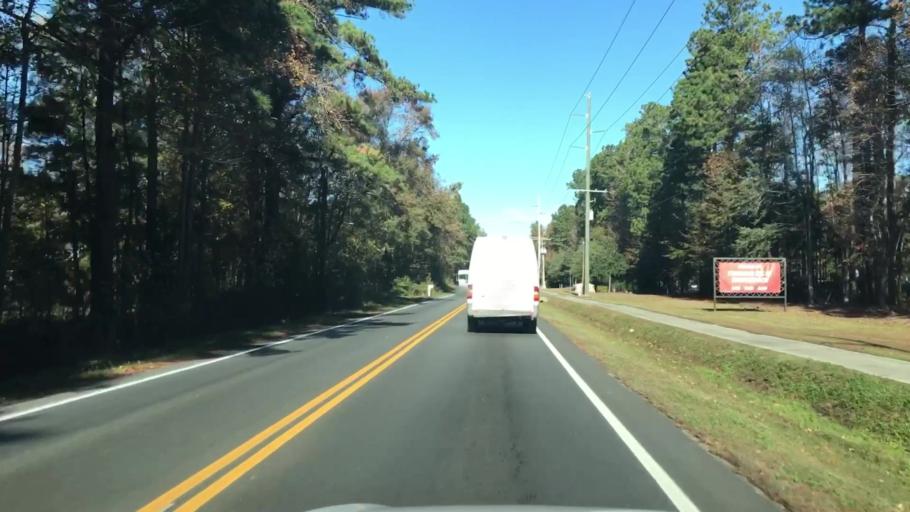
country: US
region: South Carolina
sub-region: Dorchester County
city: Summerville
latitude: 33.0004
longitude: -80.2311
